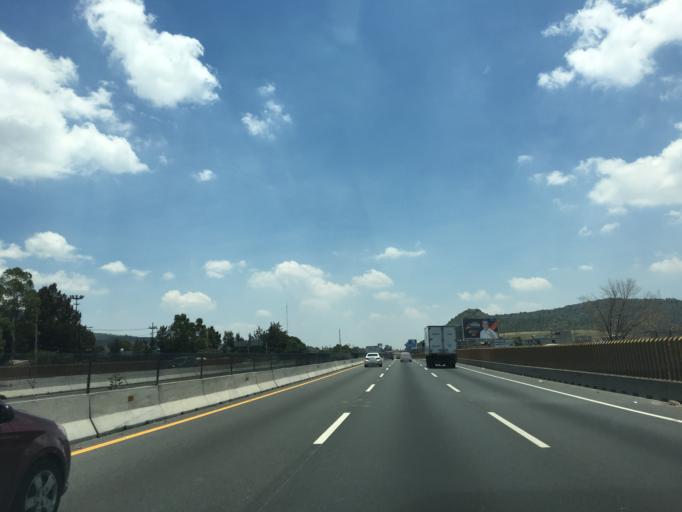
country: MX
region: Mexico
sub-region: La Paz
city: San Isidro
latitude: 19.3222
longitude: -98.9565
